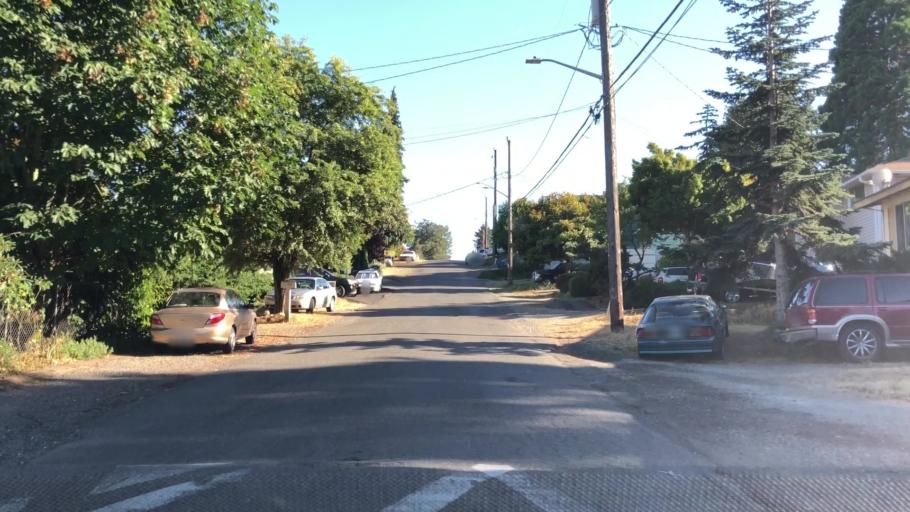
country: US
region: Washington
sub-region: King County
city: Boulevard Park
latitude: 47.5496
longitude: -122.2916
